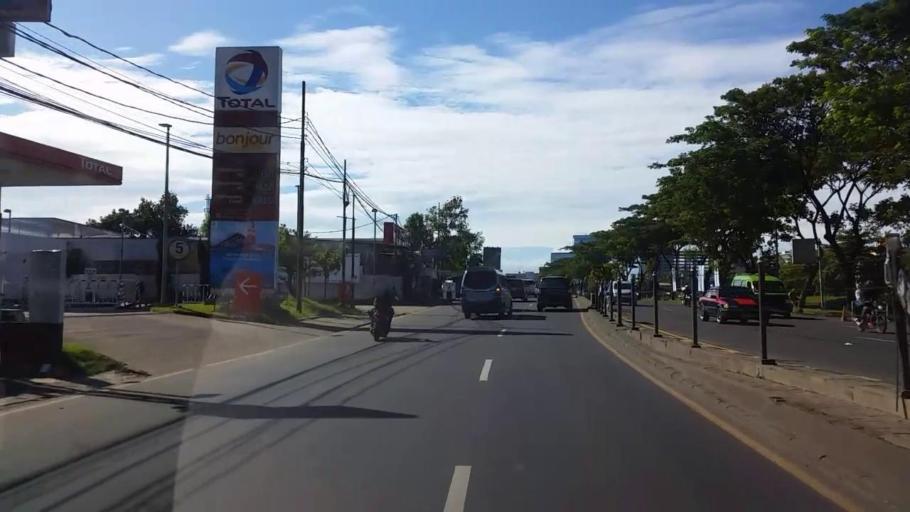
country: ID
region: West Java
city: Serpong
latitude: -6.2871
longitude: 106.6655
